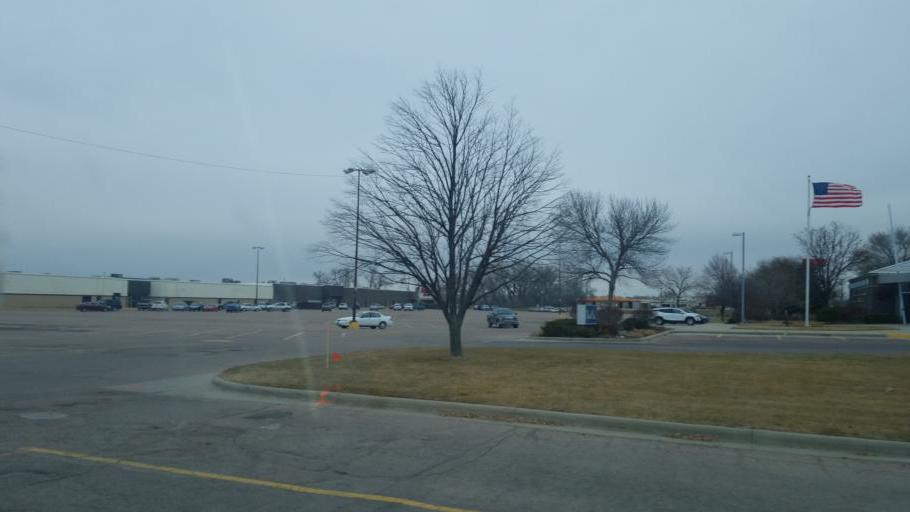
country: US
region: South Dakota
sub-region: Yankton County
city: Yankton
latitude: 42.8915
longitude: -97.3985
